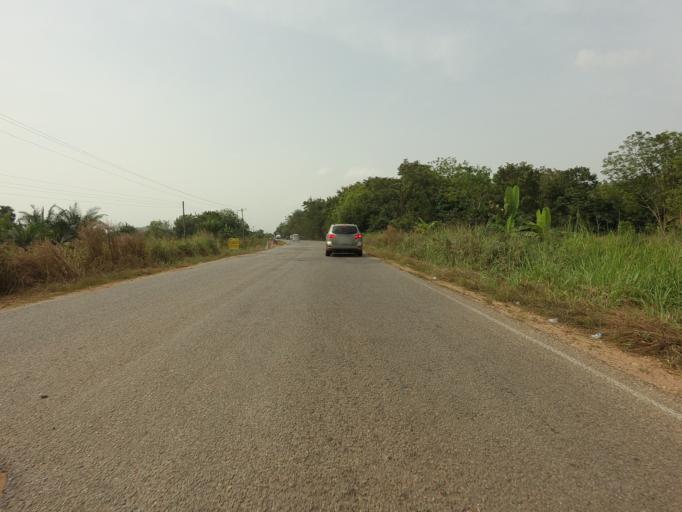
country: GH
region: Volta
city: Ho
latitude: 6.3636
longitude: 0.1814
